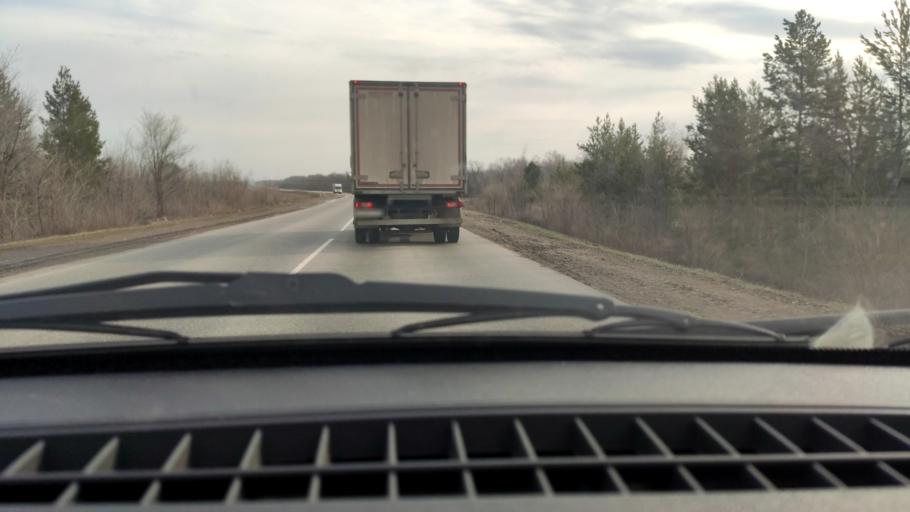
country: RU
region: Bashkortostan
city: Davlekanovo
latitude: 54.2464
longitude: 55.0762
